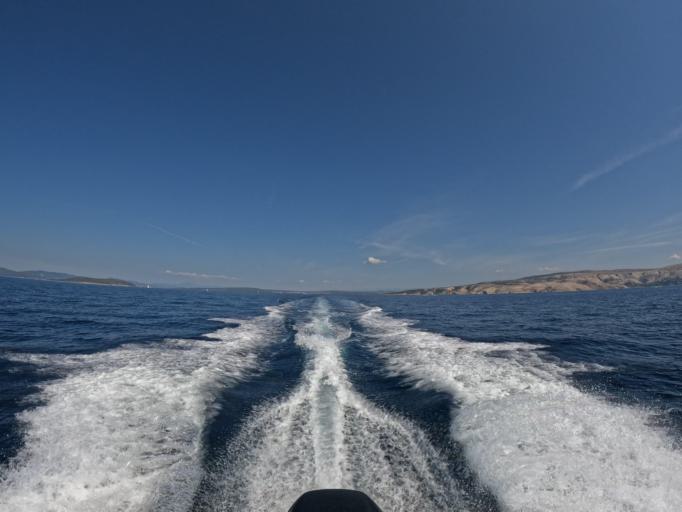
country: HR
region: Primorsko-Goranska
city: Punat
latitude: 44.9253
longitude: 14.6199
